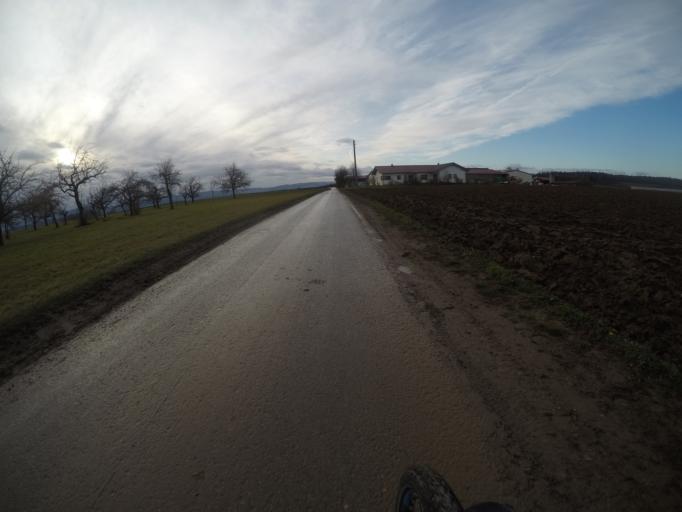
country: DE
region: Baden-Wuerttemberg
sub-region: Regierungsbezirk Stuttgart
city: Denkendorf
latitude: 48.6867
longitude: 9.3404
